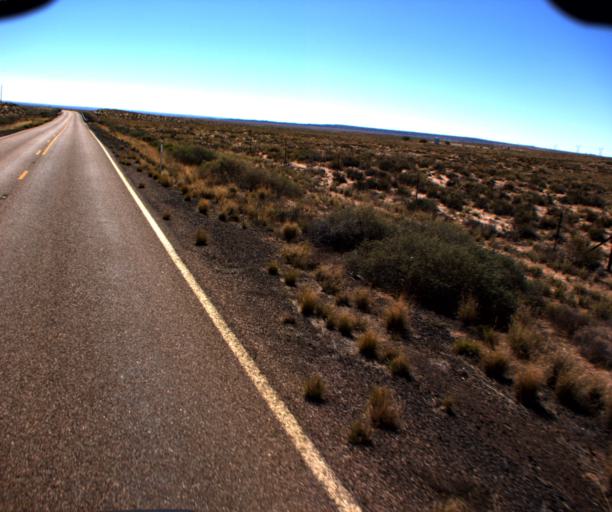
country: US
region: Arizona
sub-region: Navajo County
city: Holbrook
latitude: 35.1458
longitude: -110.0880
